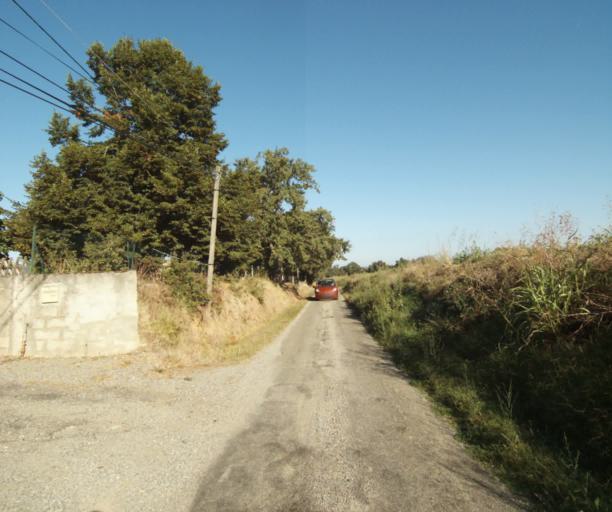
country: FR
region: Midi-Pyrenees
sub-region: Departement du Tarn-et-Garonne
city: Verdun-sur-Garonne
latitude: 43.8590
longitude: 1.2171
